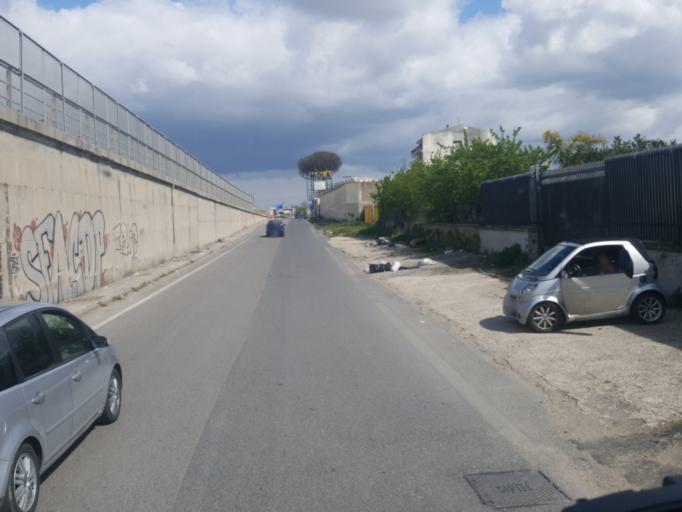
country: IT
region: Campania
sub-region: Provincia di Napoli
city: Torretta-Scalzapecora
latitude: 40.9310
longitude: 14.1122
